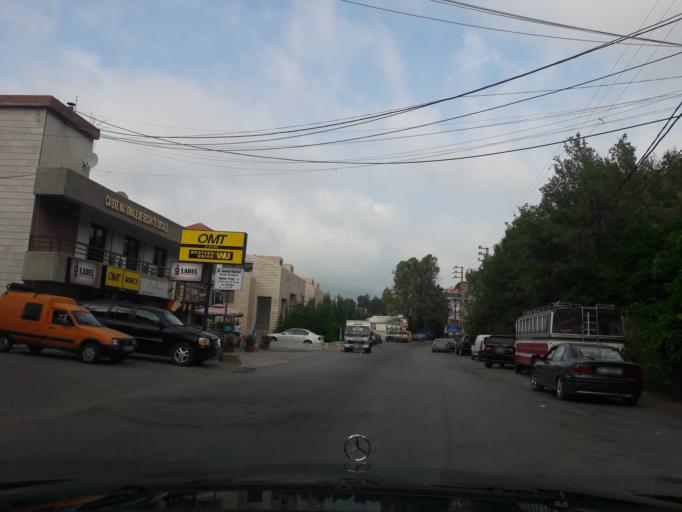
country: LB
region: Mont-Liban
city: Djounie
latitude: 33.9275
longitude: 35.7387
